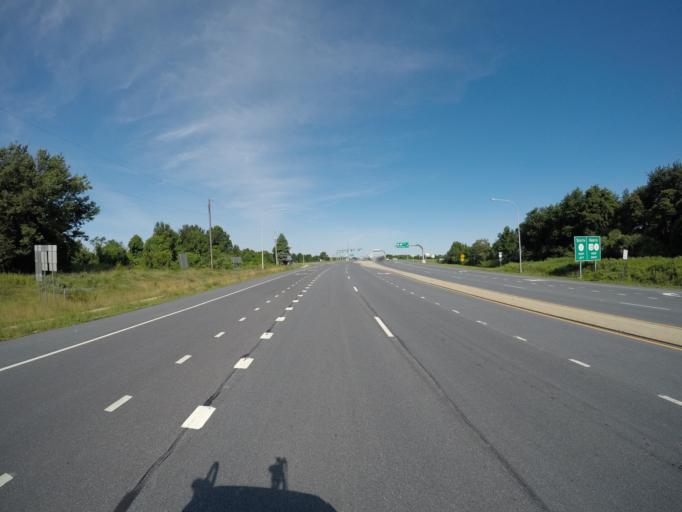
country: US
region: Delaware
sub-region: New Castle County
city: Bear
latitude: 39.5795
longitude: -75.6586
